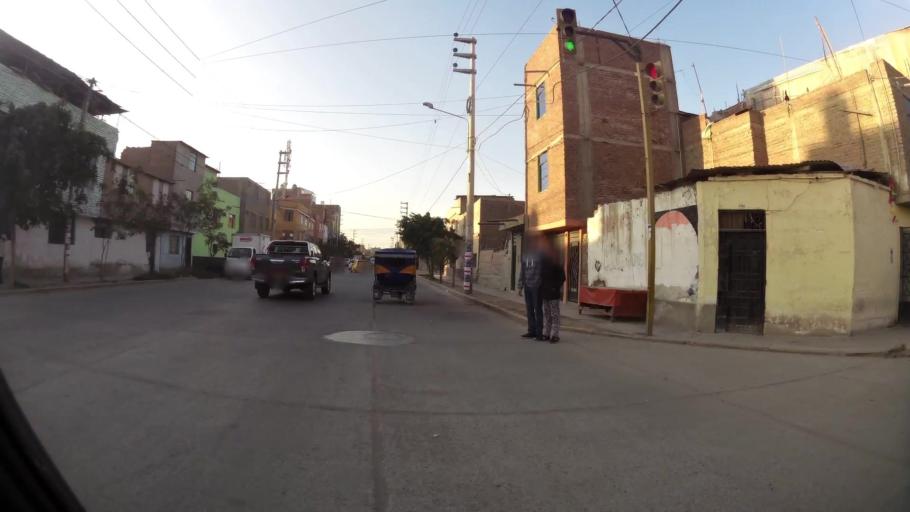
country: PE
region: Lambayeque
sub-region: Provincia de Chiclayo
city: Santa Rosa
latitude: -6.7698
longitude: -79.8297
